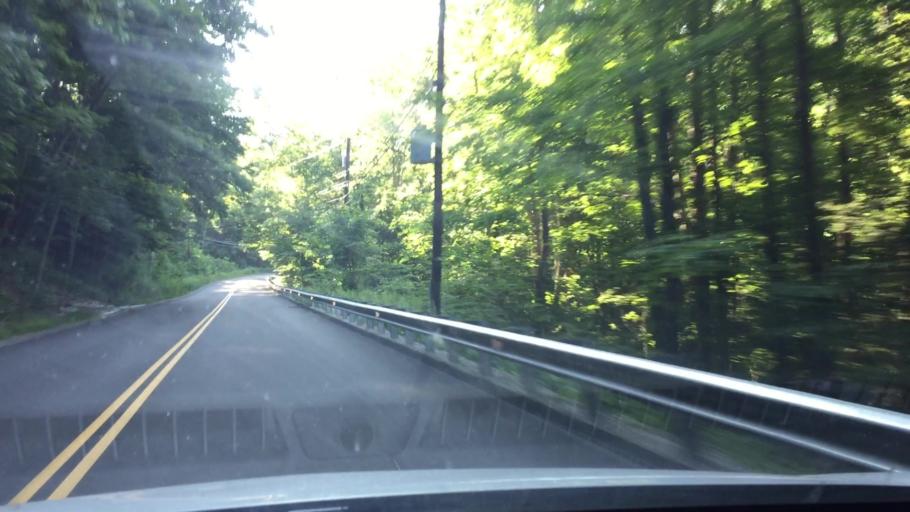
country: US
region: Massachusetts
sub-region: Berkshire County
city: Lee
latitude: 42.2926
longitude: -73.2196
